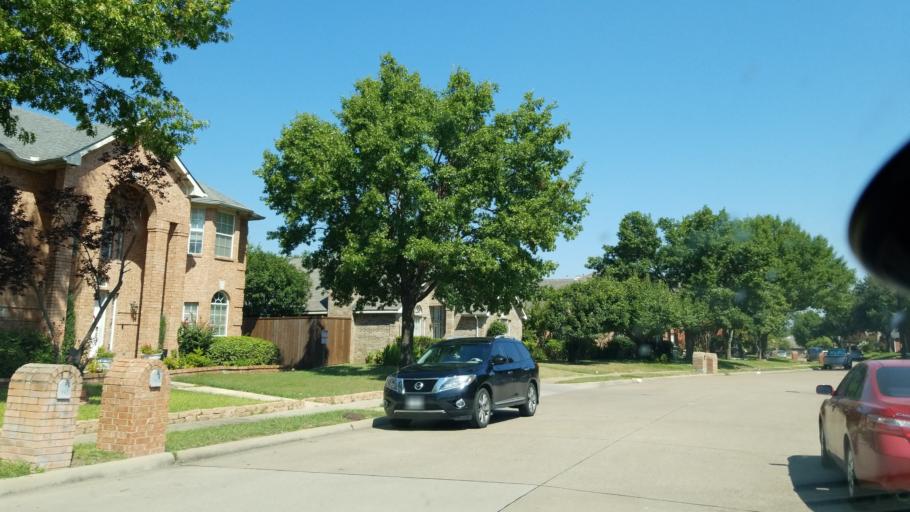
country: US
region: Texas
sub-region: Dallas County
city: Richardson
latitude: 32.9097
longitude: -96.7098
